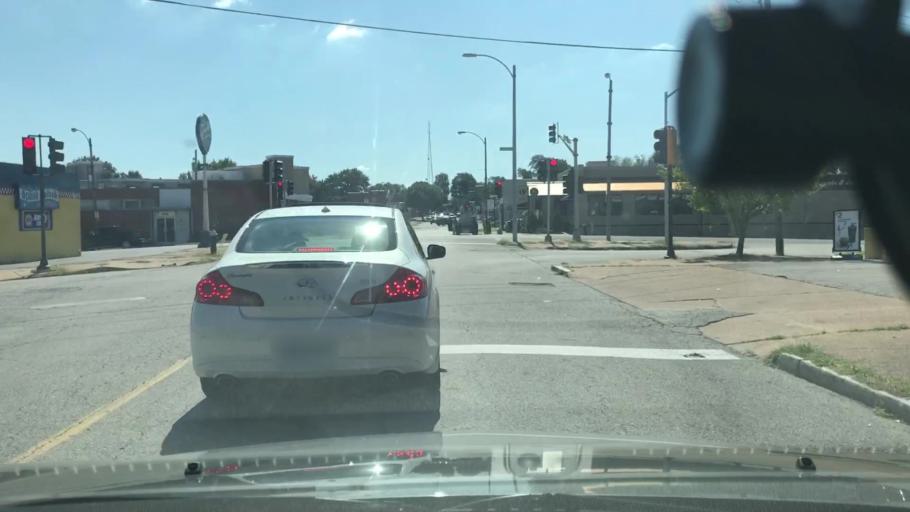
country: US
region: Missouri
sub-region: Saint Louis County
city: Maplewood
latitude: 38.6100
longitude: -90.2899
